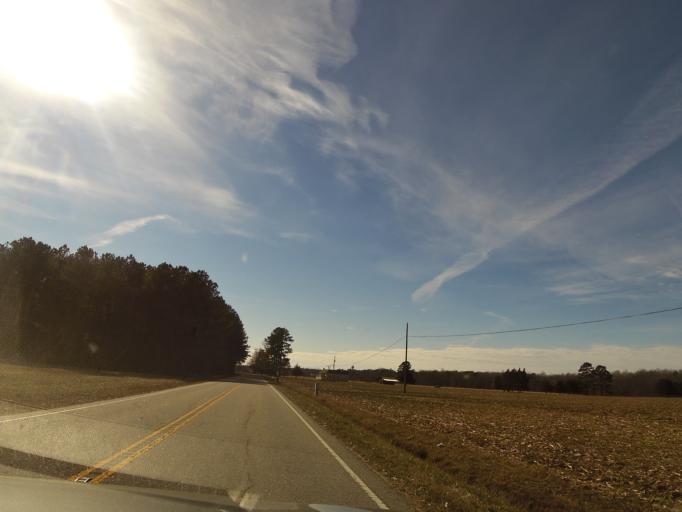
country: US
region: Virginia
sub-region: Isle of Wight County
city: Isle of Wight
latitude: 36.9207
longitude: -76.6927
